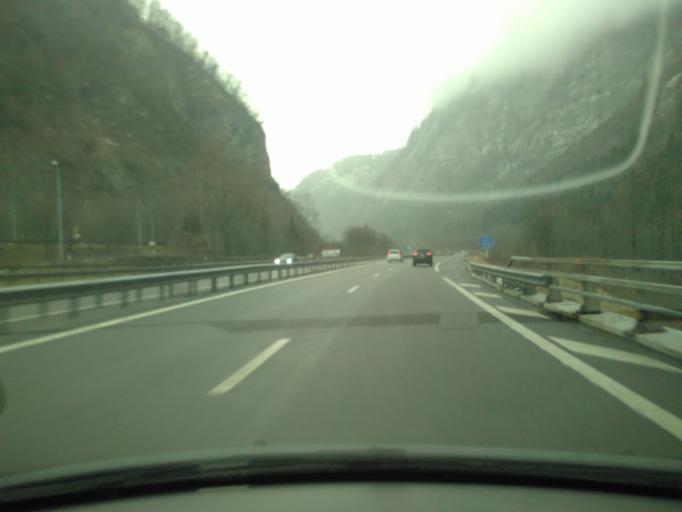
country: FR
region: Rhone-Alpes
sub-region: Departement de la Haute-Savoie
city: Cluses
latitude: 46.0540
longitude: 6.5808
